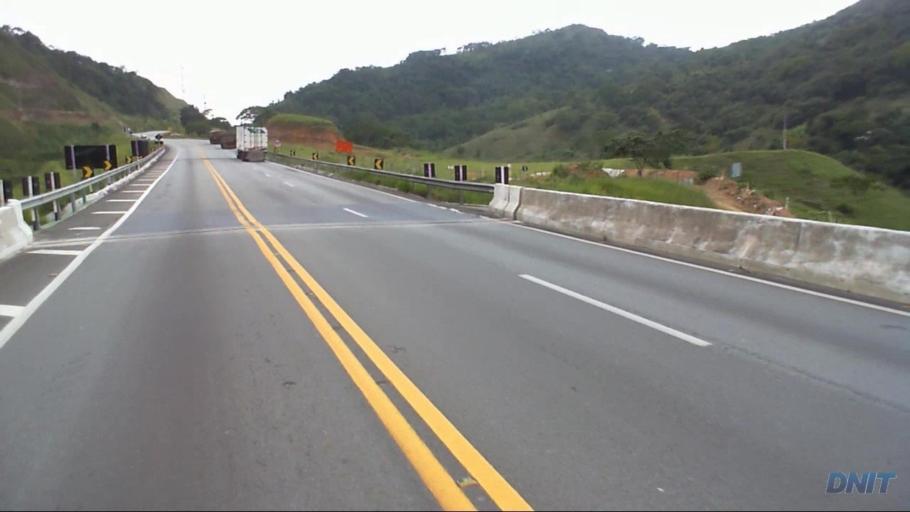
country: BR
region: Minas Gerais
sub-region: Nova Era
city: Nova Era
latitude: -19.6541
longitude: -42.9536
